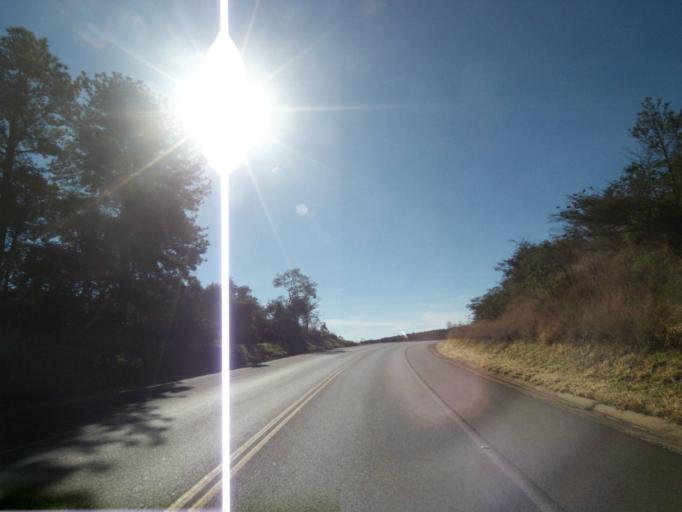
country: BR
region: Parana
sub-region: Tibagi
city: Tibagi
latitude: -24.4081
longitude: -50.3525
